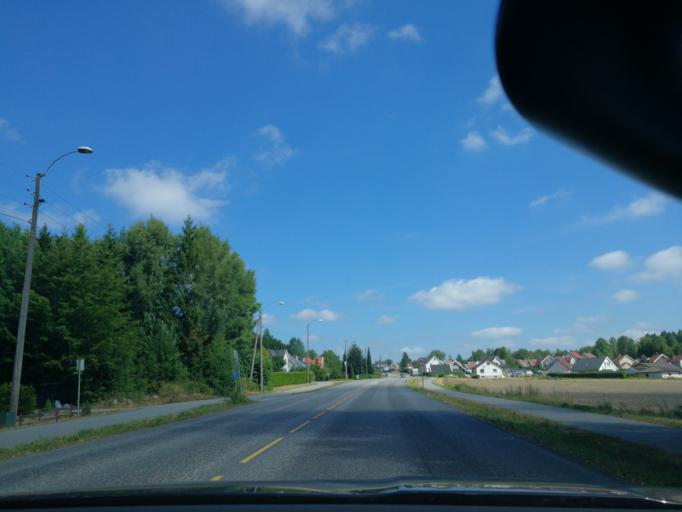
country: NO
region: Vestfold
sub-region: Sandefjord
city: Sandefjord
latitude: 59.1697
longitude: 10.2088
